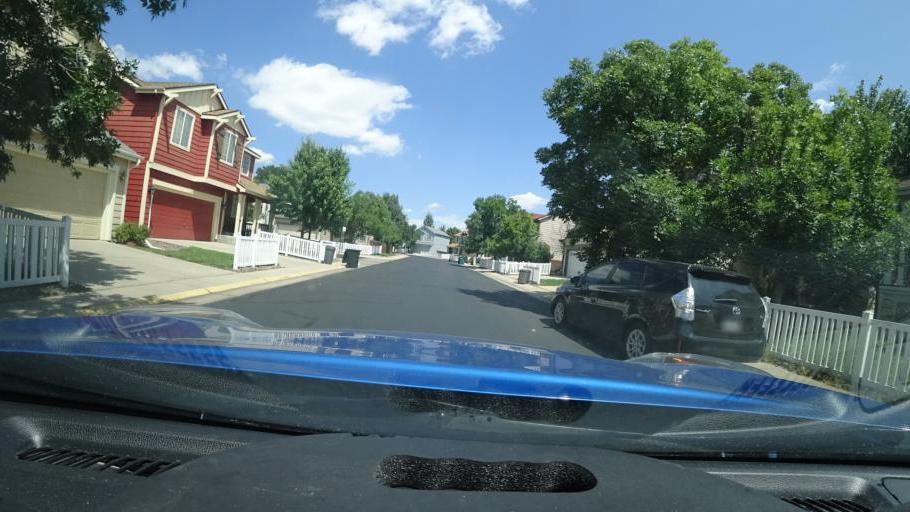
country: US
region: Colorado
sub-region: Arapahoe County
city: Glendale
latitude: 39.6937
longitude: -104.8781
